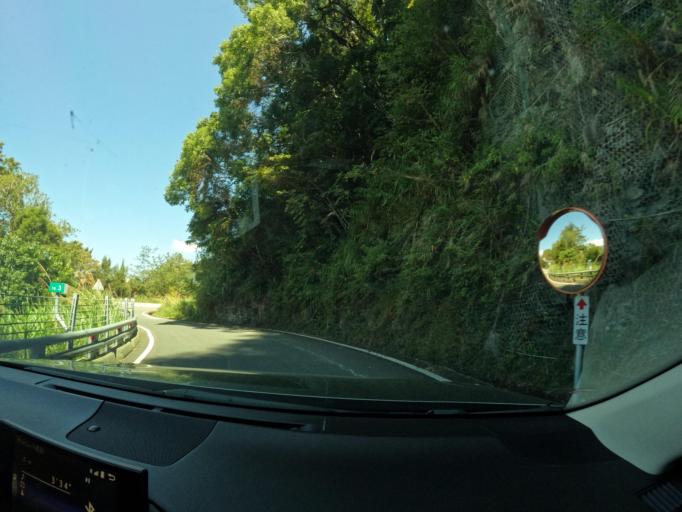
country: TW
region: Taiwan
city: Yujing
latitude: 23.2847
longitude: 120.8781
